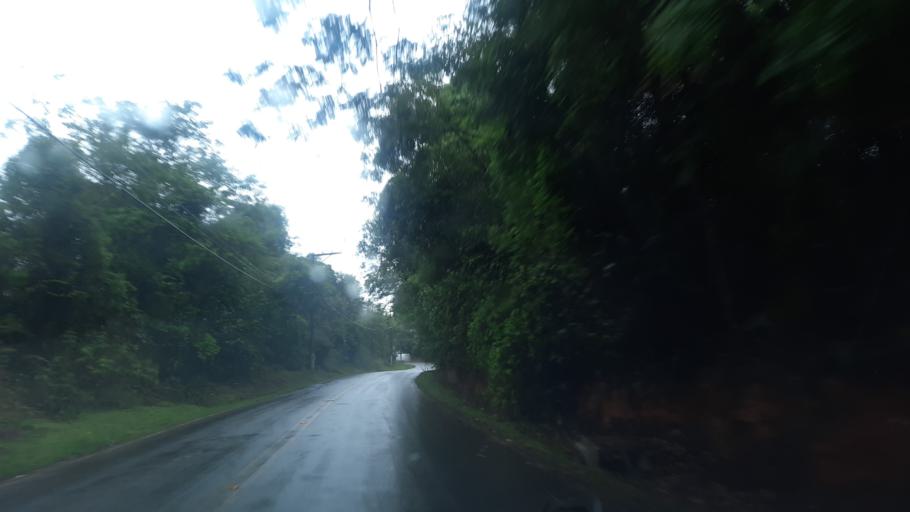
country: BR
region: Sao Paulo
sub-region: Atibaia
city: Atibaia
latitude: -23.0765
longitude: -46.5207
